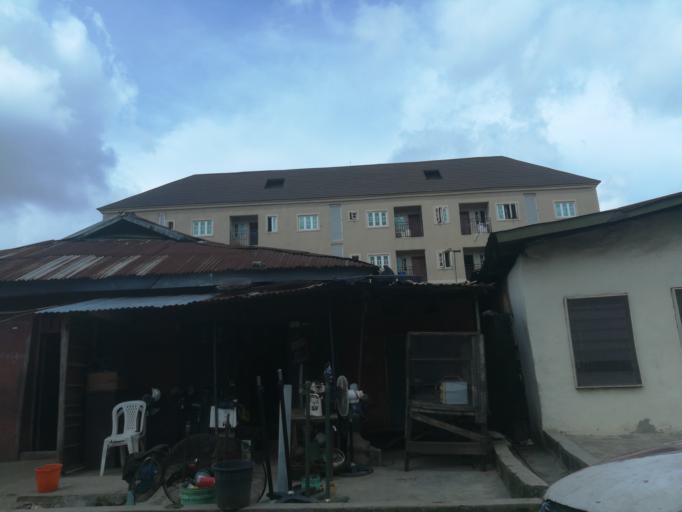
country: NG
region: Lagos
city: Somolu
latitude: 6.5307
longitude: 3.3819
